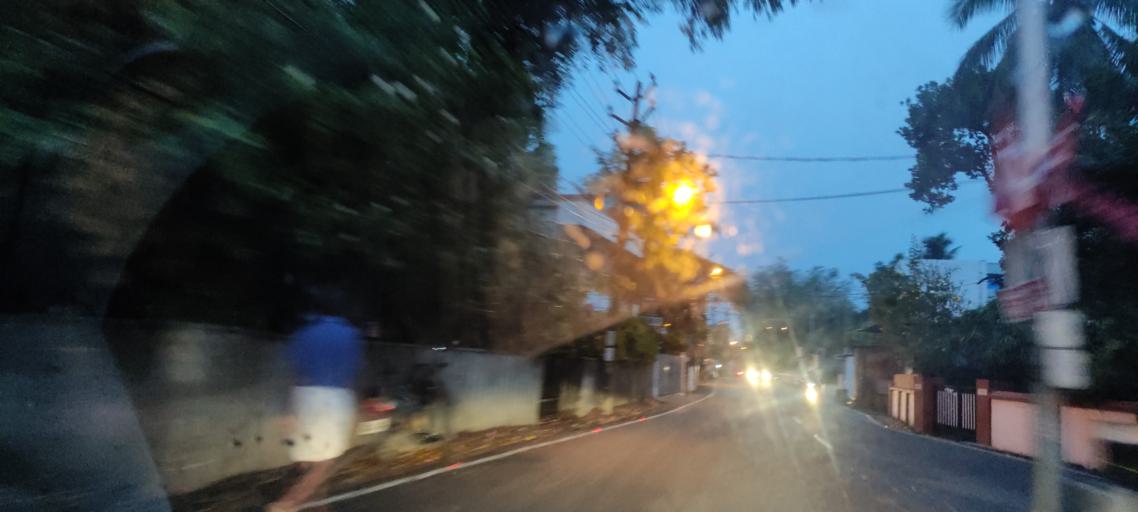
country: IN
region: Kerala
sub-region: Ernakulam
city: Cochin
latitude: 9.9120
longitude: 76.2938
